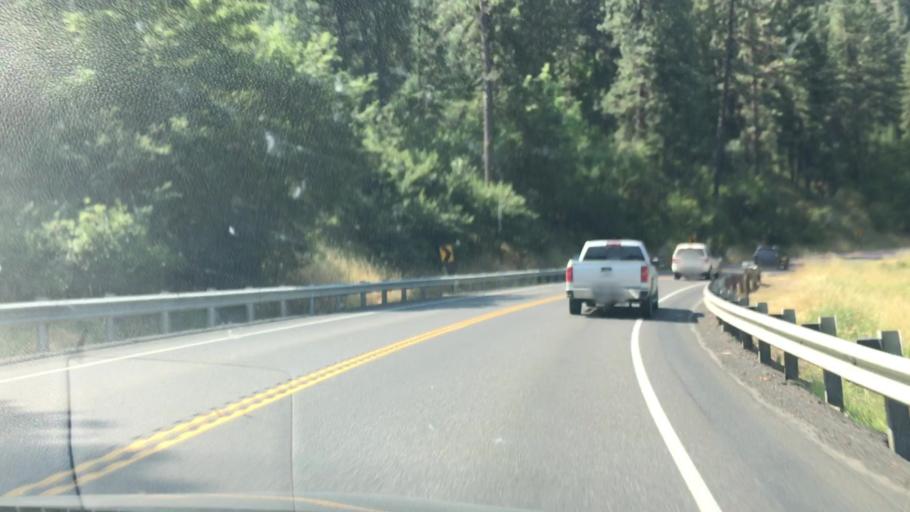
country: US
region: Idaho
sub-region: Clearwater County
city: Orofino
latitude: 46.4906
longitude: -116.4499
